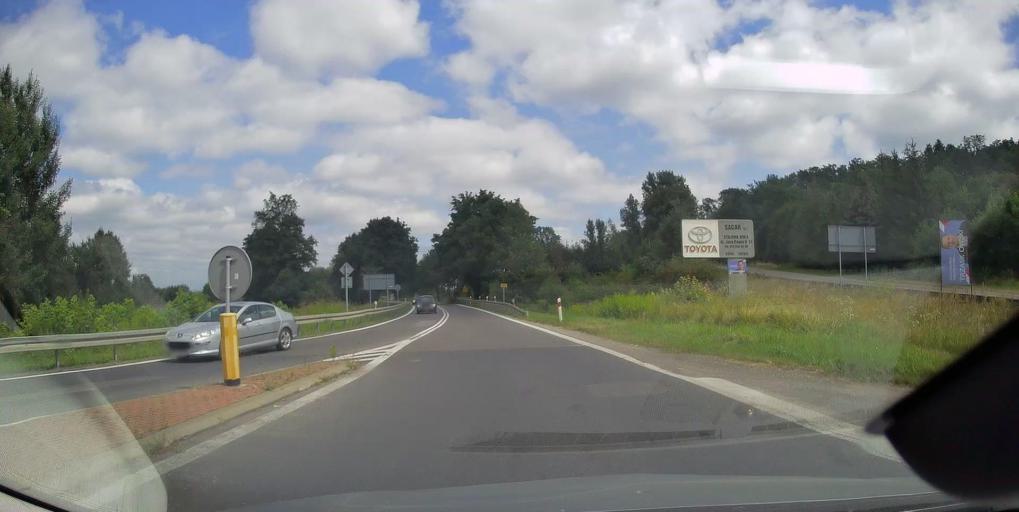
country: PL
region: Subcarpathian Voivodeship
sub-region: Powiat tarnobrzeski
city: Baranow Sandomierski
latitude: 50.4861
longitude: 21.5667
